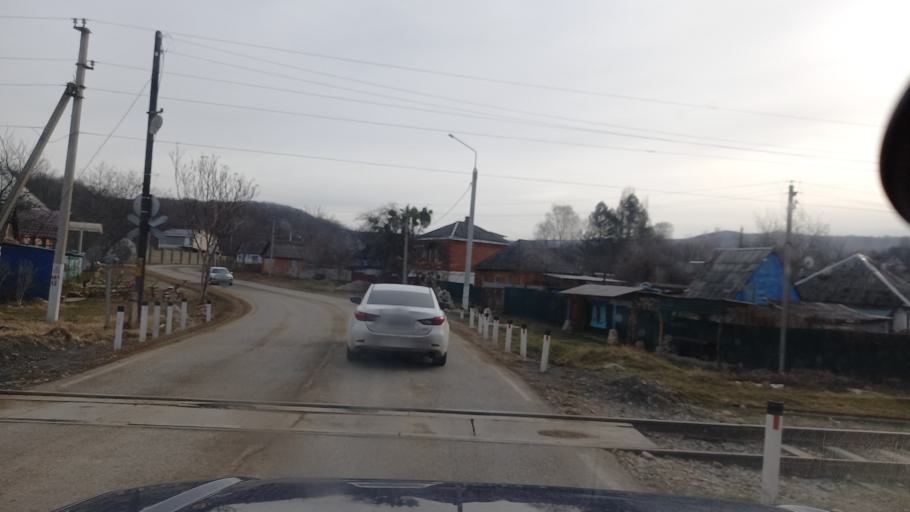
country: RU
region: Adygeya
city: Kamennomostskiy
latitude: 44.2970
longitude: 40.1885
